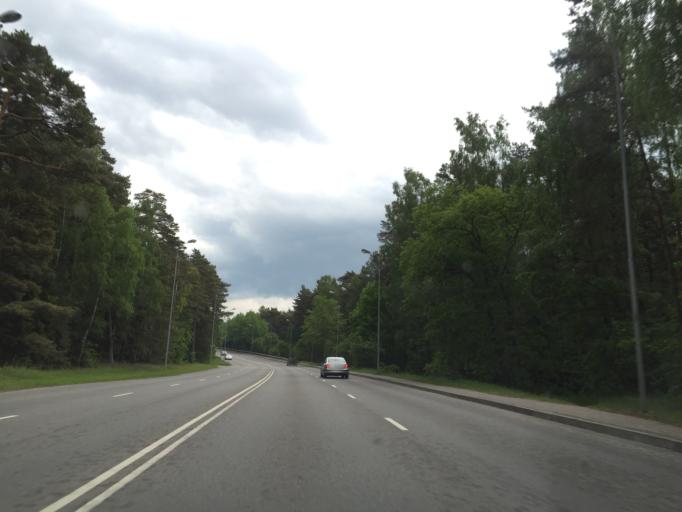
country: LT
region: Klaipedos apskritis
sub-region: Klaipeda
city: Klaipeda
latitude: 55.7356
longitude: 21.0999
